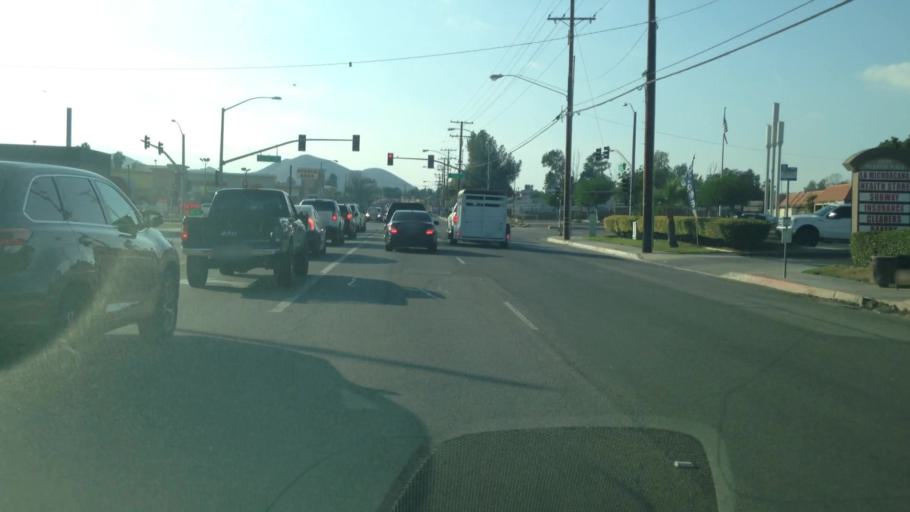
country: US
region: California
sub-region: Riverside County
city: Pedley
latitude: 33.9466
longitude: -117.4766
